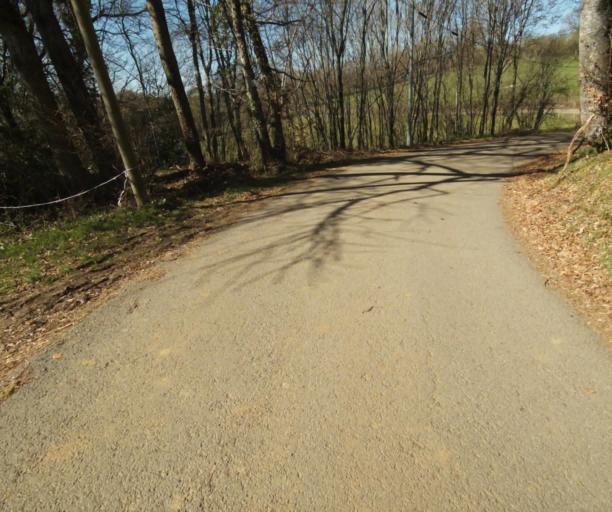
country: FR
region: Limousin
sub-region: Departement de la Correze
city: Chamboulive
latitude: 45.4162
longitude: 1.6719
